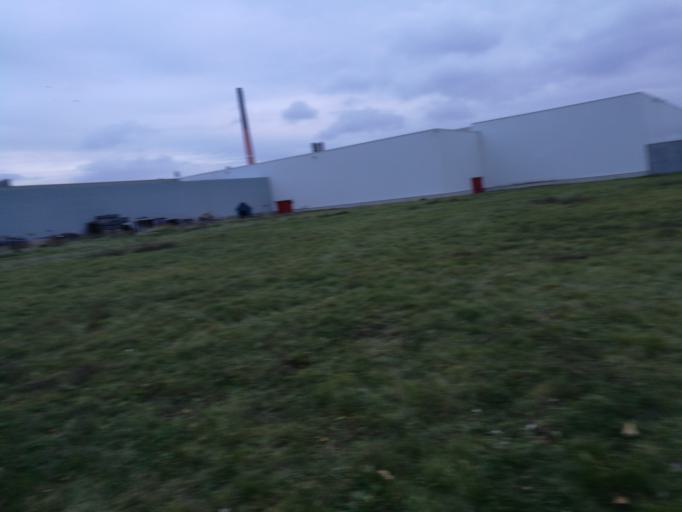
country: RO
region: Suceava
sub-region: Comuna Scheia
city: Scheia
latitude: 47.6668
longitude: 26.2667
